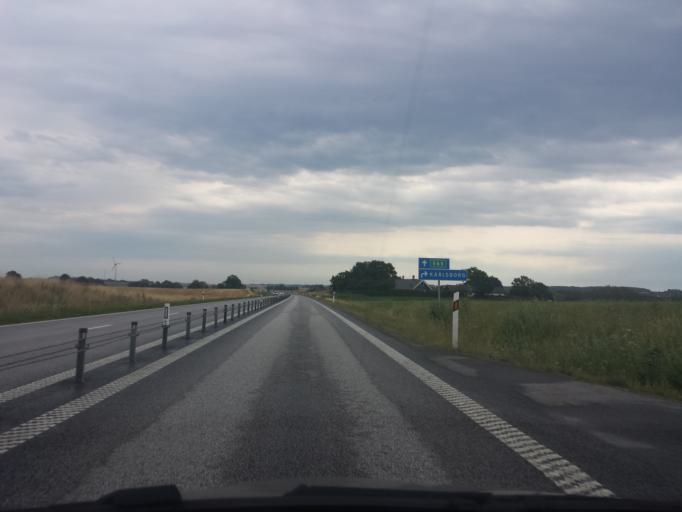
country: SE
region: Skane
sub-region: Skurups Kommun
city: Rydsgard
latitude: 55.4769
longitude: 13.6411
